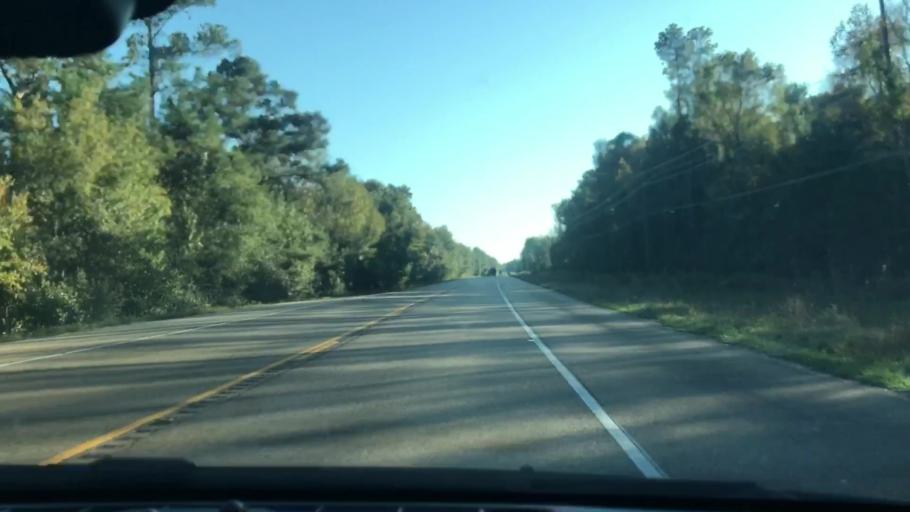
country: US
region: Louisiana
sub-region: Saint Tammany Parish
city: Abita Springs
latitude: 30.5583
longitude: -89.8719
